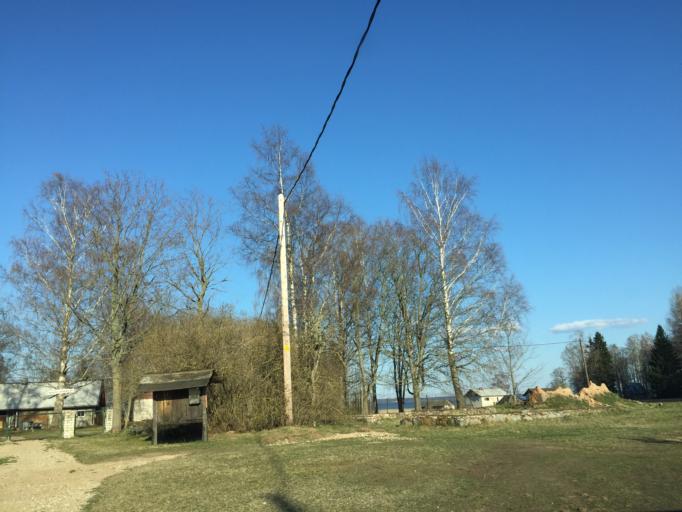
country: EE
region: Valgamaa
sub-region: Torva linn
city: Torva
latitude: 58.2260
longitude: 25.9779
